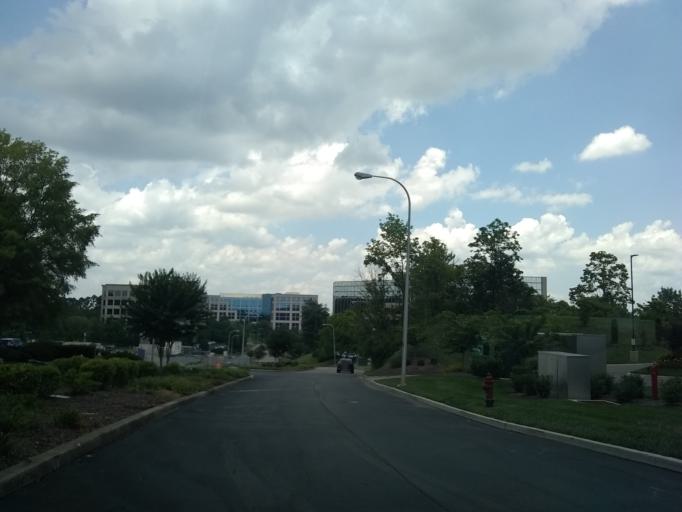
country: US
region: Tennessee
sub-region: Davidson County
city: Nashville
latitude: 36.1445
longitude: -86.6864
